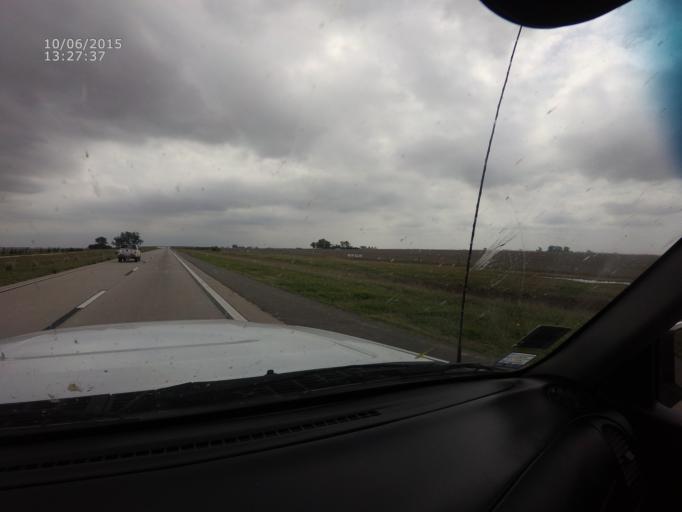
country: AR
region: Cordoba
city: Leones
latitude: -32.6451
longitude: -62.2063
